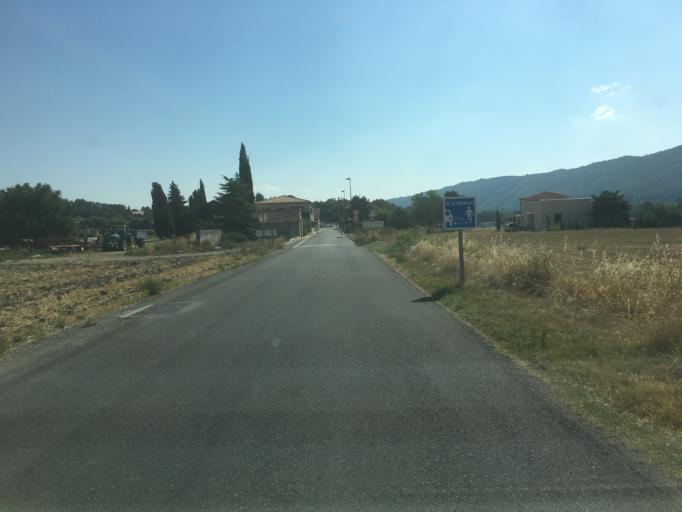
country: FR
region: Provence-Alpes-Cote d'Azur
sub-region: Departement des Alpes-de-Haute-Provence
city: Oraison
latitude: 43.8848
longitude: 5.9103
